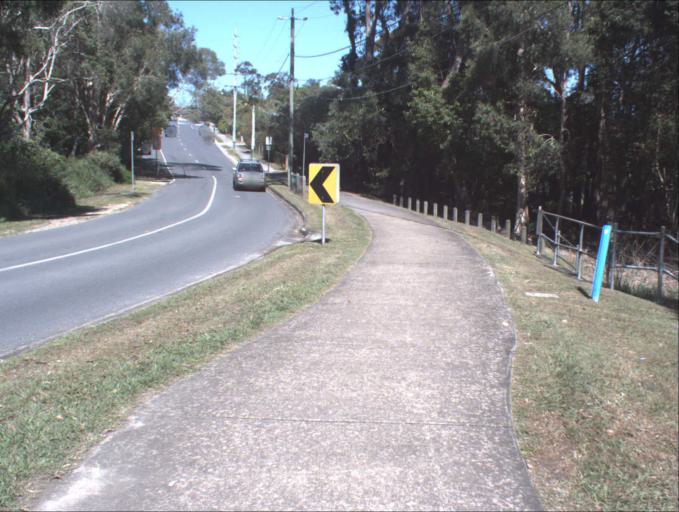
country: AU
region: Queensland
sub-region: Logan
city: Springwood
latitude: -27.6150
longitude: 153.1447
